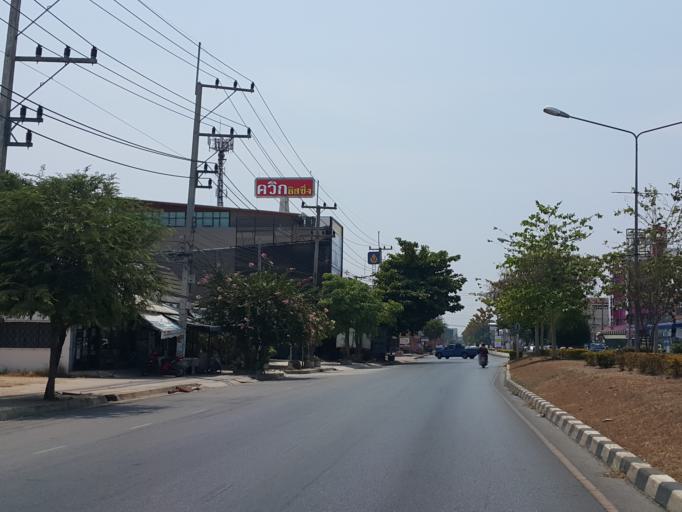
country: TH
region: Kanchanaburi
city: Kanchanaburi
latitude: 14.0371
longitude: 99.5202
